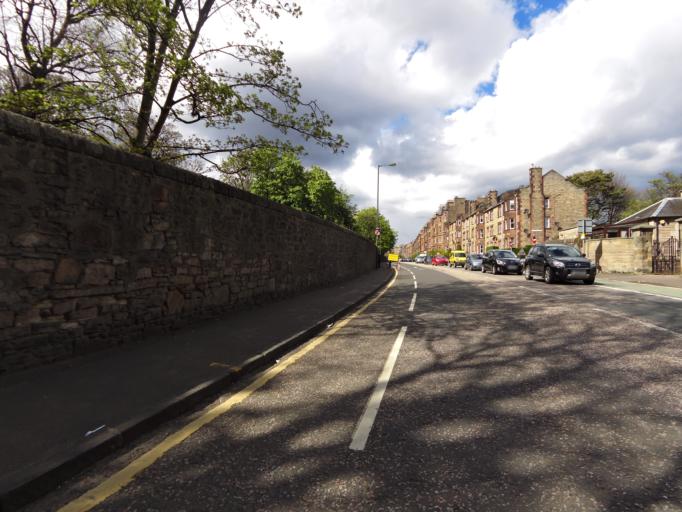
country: GB
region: Scotland
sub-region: West Lothian
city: Seafield
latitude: 55.9305
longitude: -3.1628
